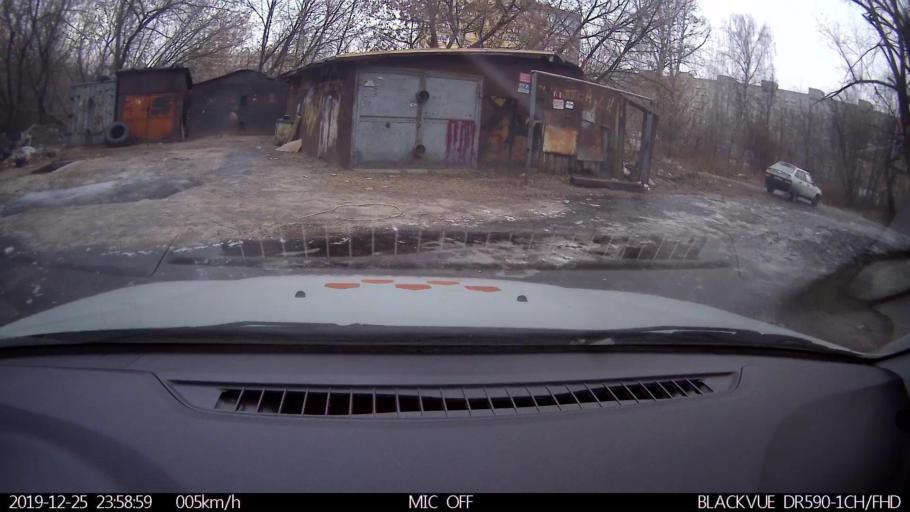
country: RU
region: Nizjnij Novgorod
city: Gorbatovka
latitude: 56.3425
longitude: 43.8282
